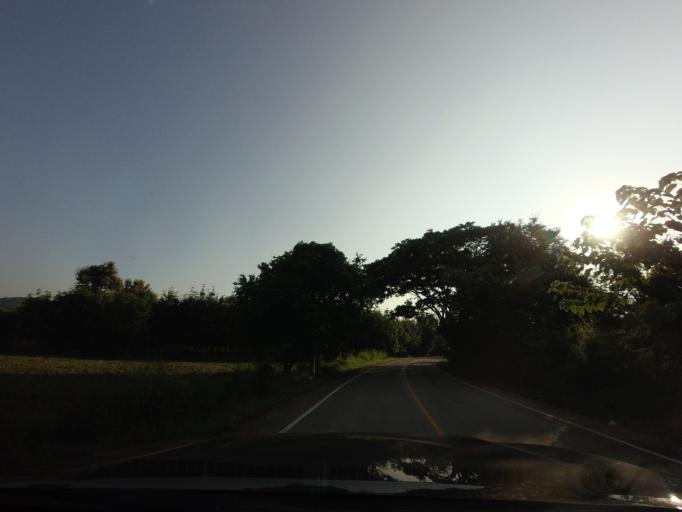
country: TH
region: Nan
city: Na Noi
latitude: 18.3065
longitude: 100.7657
